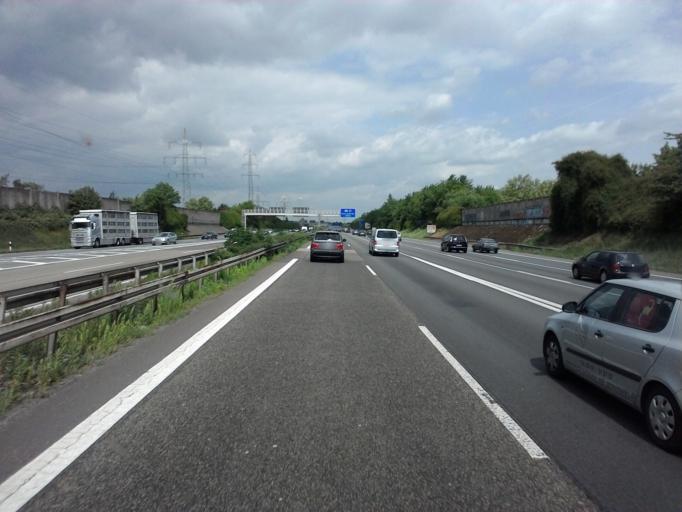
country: DE
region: North Rhine-Westphalia
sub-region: Regierungsbezirk Koln
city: Ostheim
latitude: 50.9278
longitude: 7.0563
